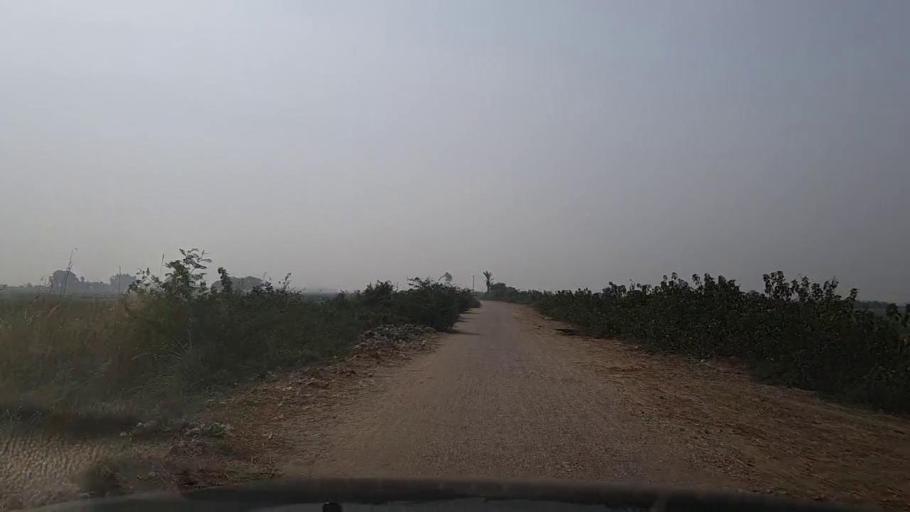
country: PK
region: Sindh
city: Mirpur Sakro
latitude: 24.5492
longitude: 67.8351
